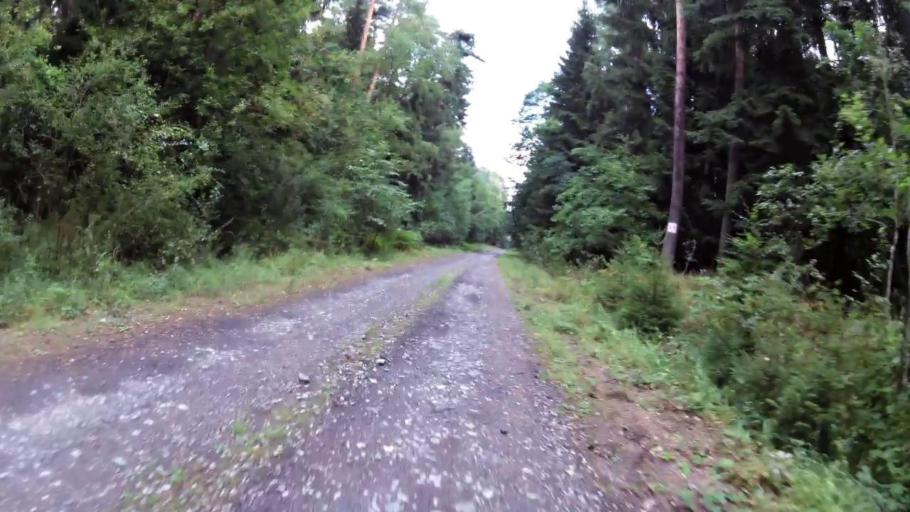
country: PL
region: West Pomeranian Voivodeship
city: Trzcinsko Zdroj
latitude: 52.8920
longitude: 14.6901
